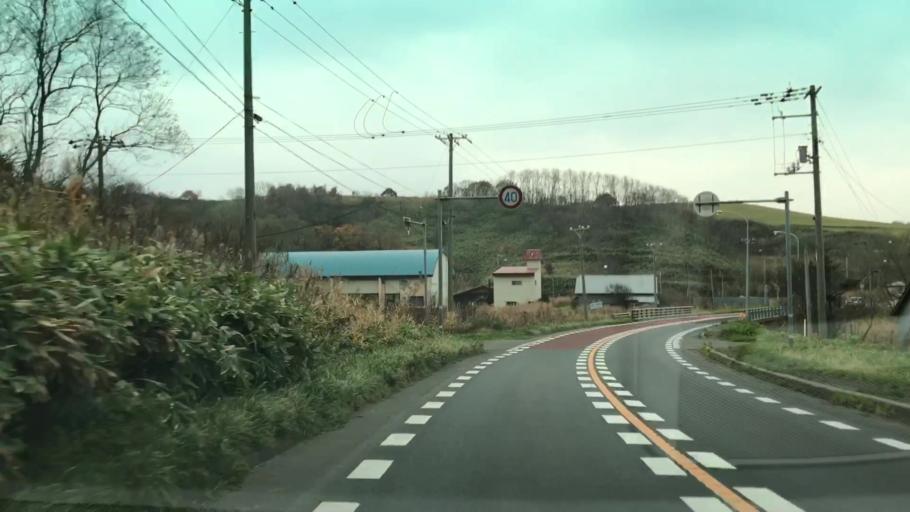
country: JP
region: Hokkaido
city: Ishikari
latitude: 43.3565
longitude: 141.4303
